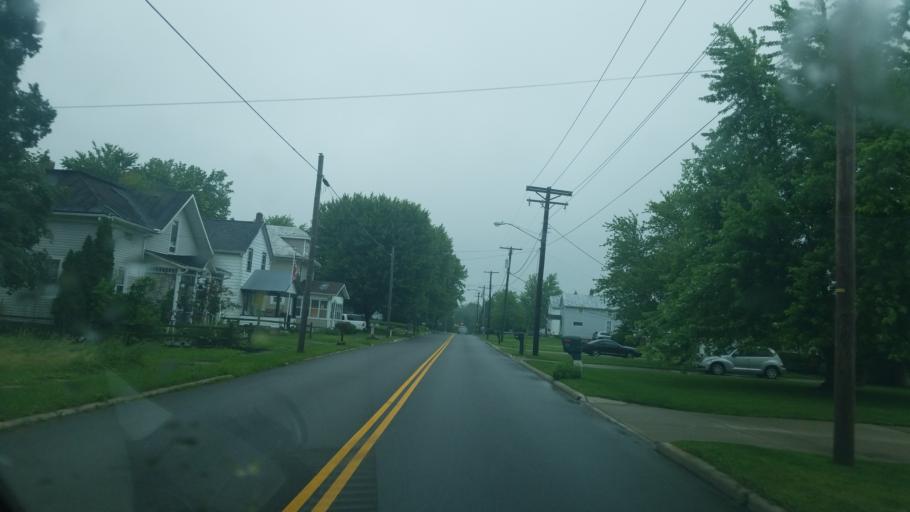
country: US
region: Ohio
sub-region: Crawford County
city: Bucyrus
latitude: 40.8081
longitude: -82.9591
